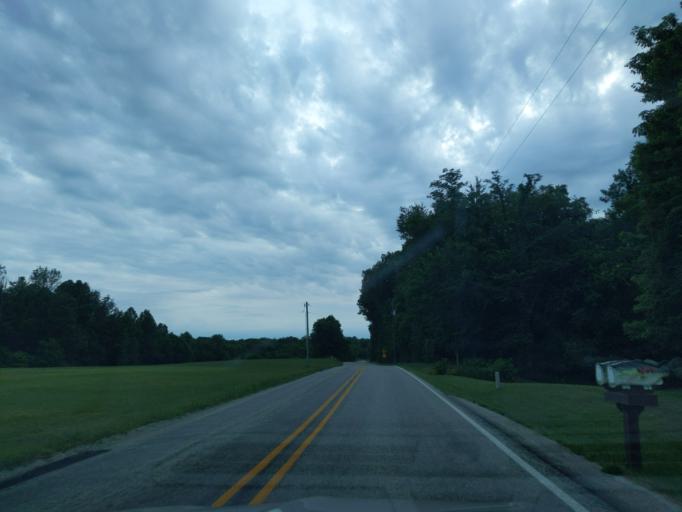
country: US
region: Indiana
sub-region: Ripley County
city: Batesville
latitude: 39.2021
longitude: -85.1953
